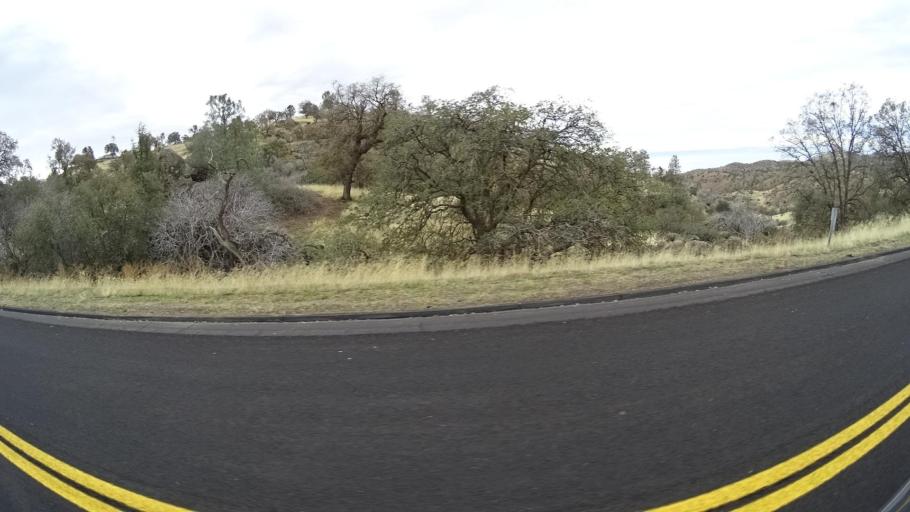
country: US
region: California
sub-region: Kern County
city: Stallion Springs
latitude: 35.1036
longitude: -118.6703
